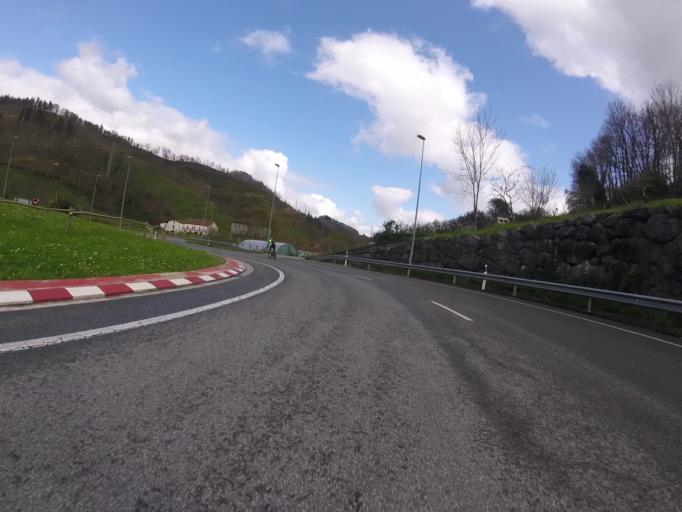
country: ES
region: Basque Country
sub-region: Provincia de Guipuzcoa
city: Amezqueta
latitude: 43.0530
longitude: -2.0883
